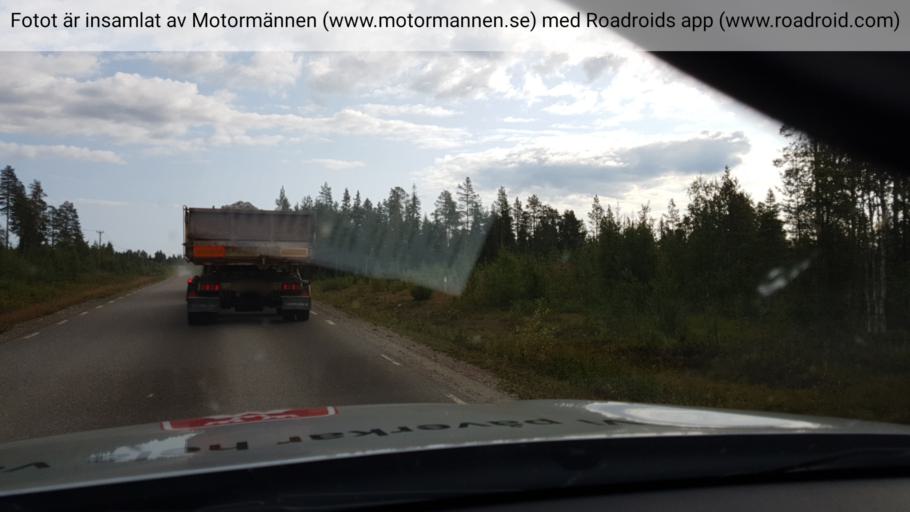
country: SE
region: Vaesterbotten
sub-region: Skelleftea Kommun
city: Storvik
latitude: 65.3876
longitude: 20.3760
